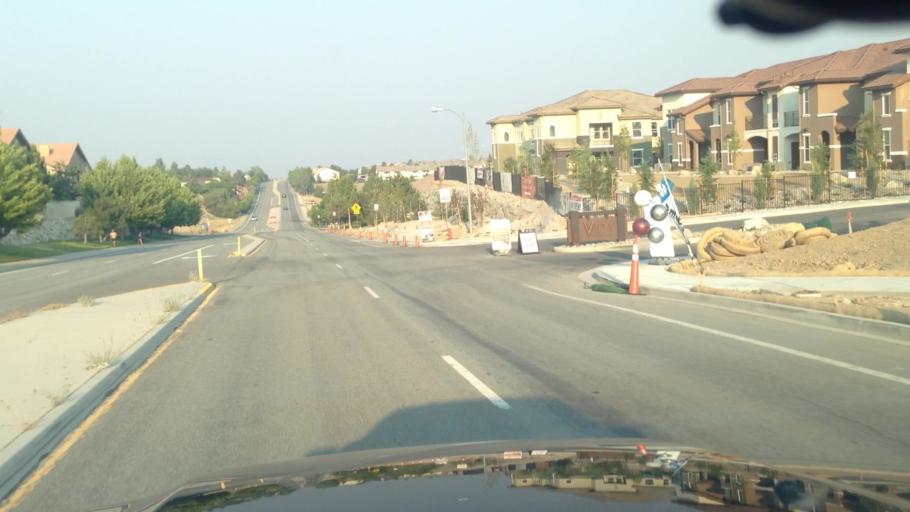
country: US
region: Nevada
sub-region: Washoe County
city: Mogul
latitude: 39.5193
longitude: -119.8994
